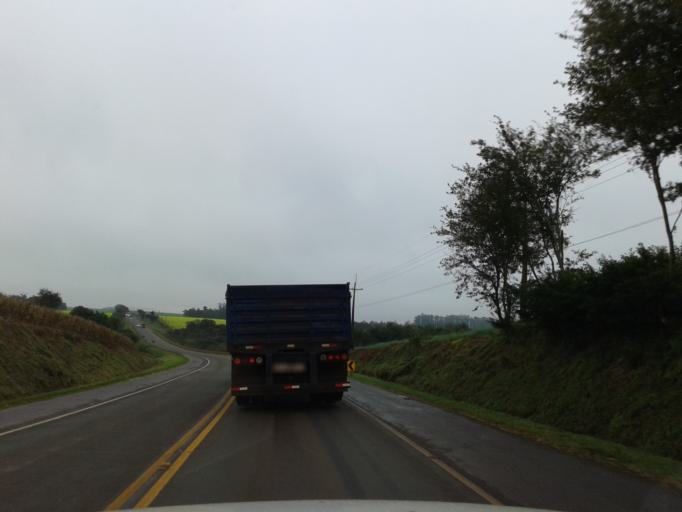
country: PY
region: Alto Parana
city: Naranjal
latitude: -25.9749
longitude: -55.1146
